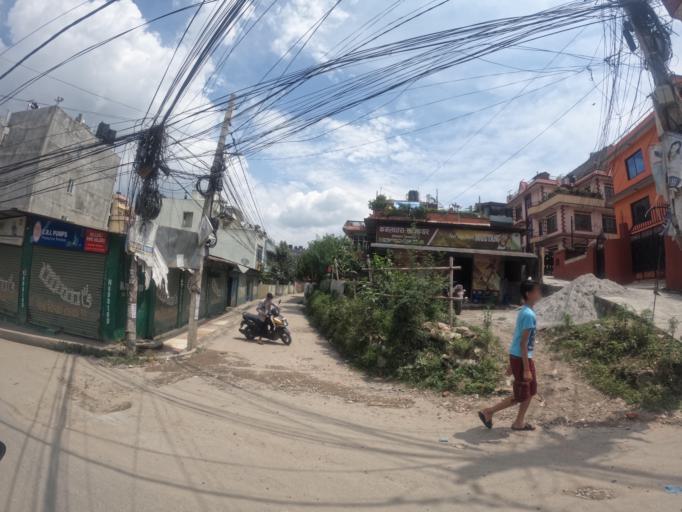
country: NP
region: Central Region
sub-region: Bagmati Zone
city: Patan
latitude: 27.6763
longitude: 85.3659
